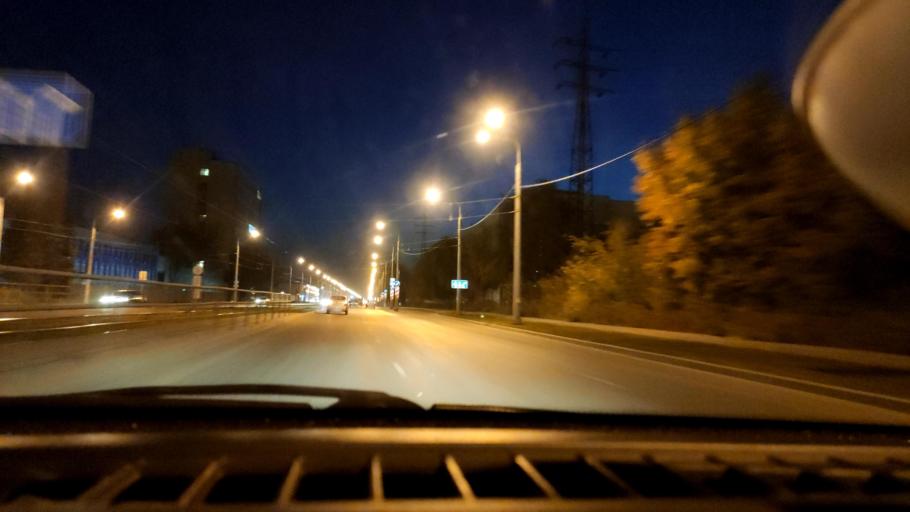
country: RU
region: Samara
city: Smyshlyayevka
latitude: 53.2059
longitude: 50.2732
